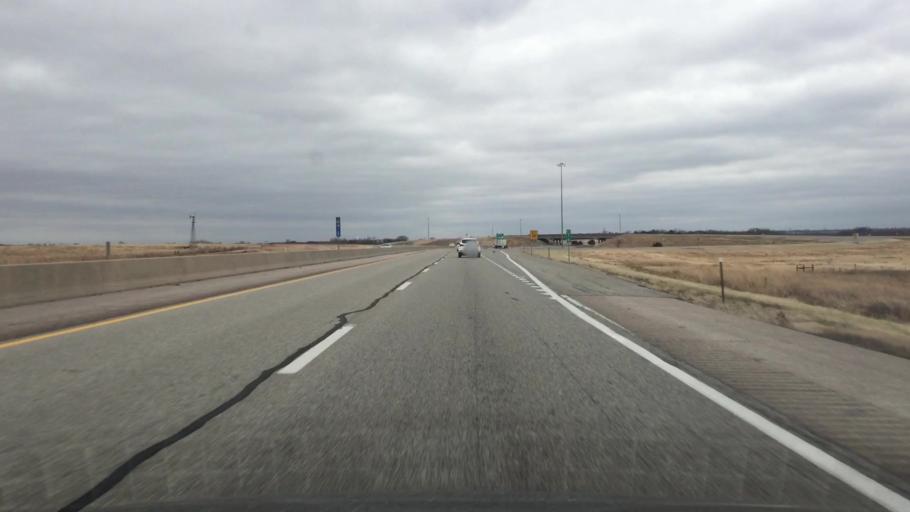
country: US
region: Kansas
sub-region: Butler County
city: El Dorado
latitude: 37.8803
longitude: -96.8431
